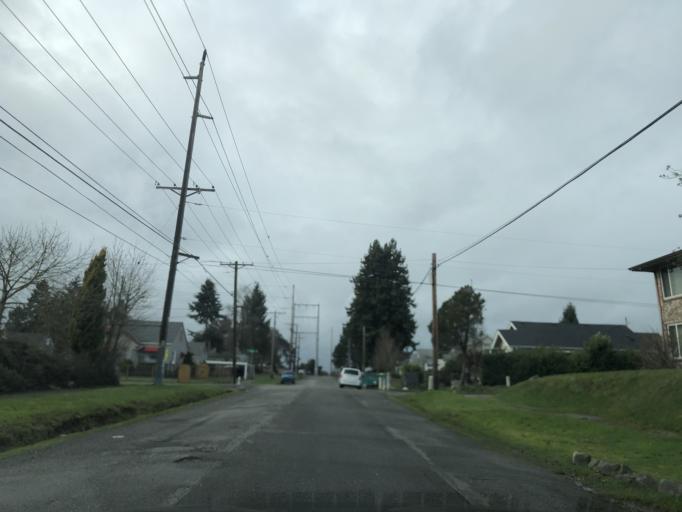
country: US
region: Washington
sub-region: Pierce County
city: Tacoma
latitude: 47.2281
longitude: -122.4572
